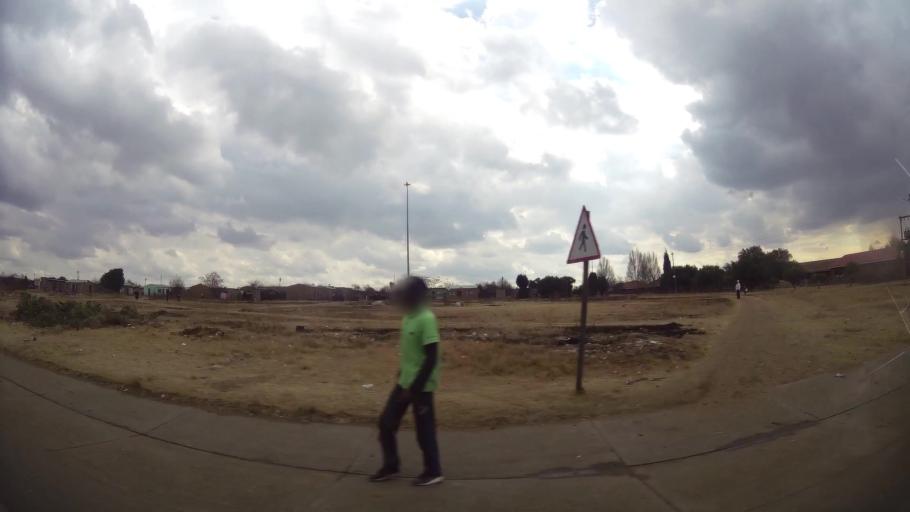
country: ZA
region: Orange Free State
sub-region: Fezile Dabi District Municipality
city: Sasolburg
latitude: -26.8522
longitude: 27.8773
